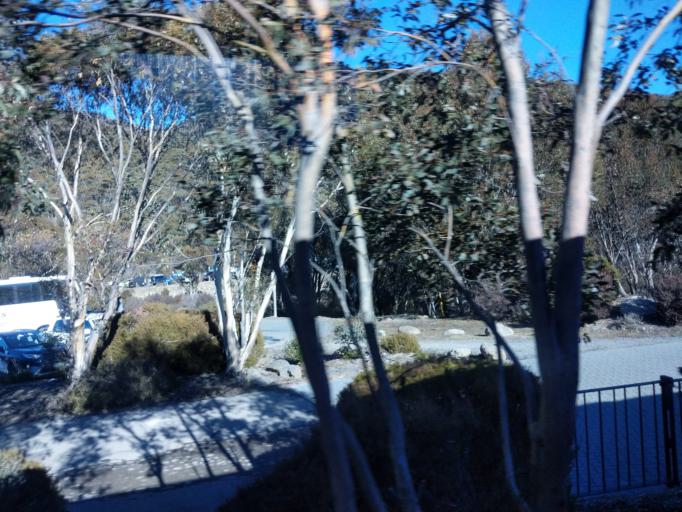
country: AU
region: New South Wales
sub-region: Snowy River
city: Jindabyne
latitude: -36.4991
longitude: 148.3120
